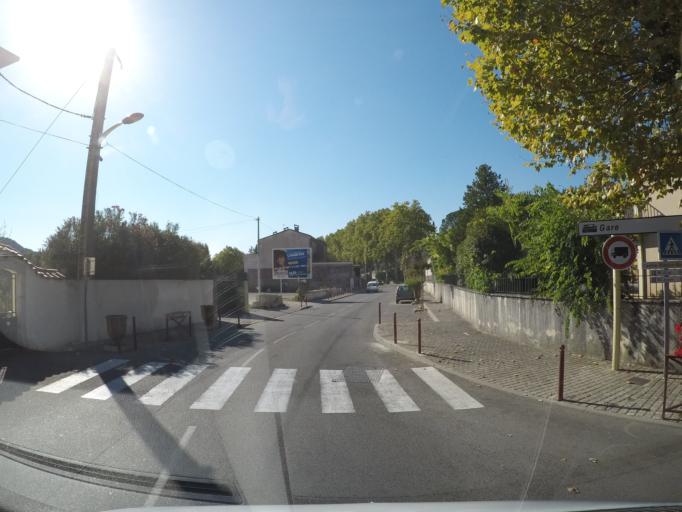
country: FR
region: Languedoc-Roussillon
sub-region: Departement du Gard
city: Anduze
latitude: 44.0507
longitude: 3.9852
